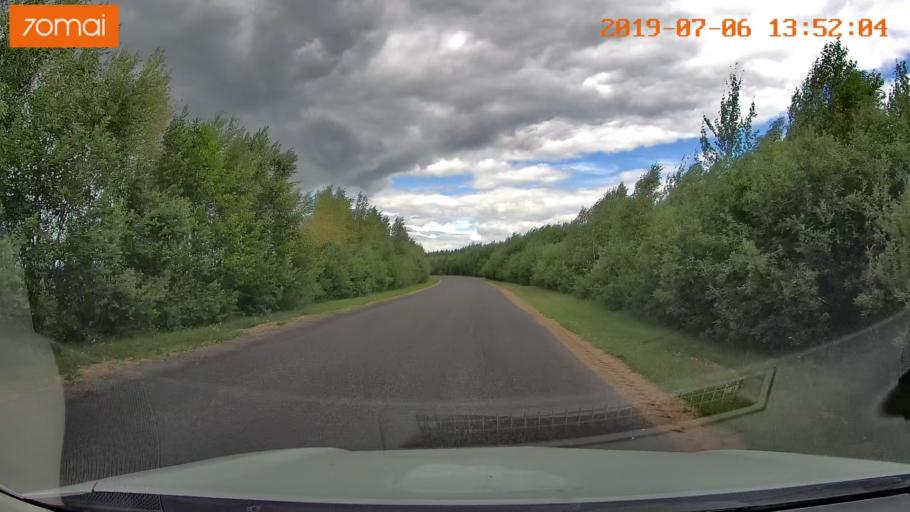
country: BY
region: Minsk
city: Ivyanyets
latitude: 53.7160
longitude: 26.8299
